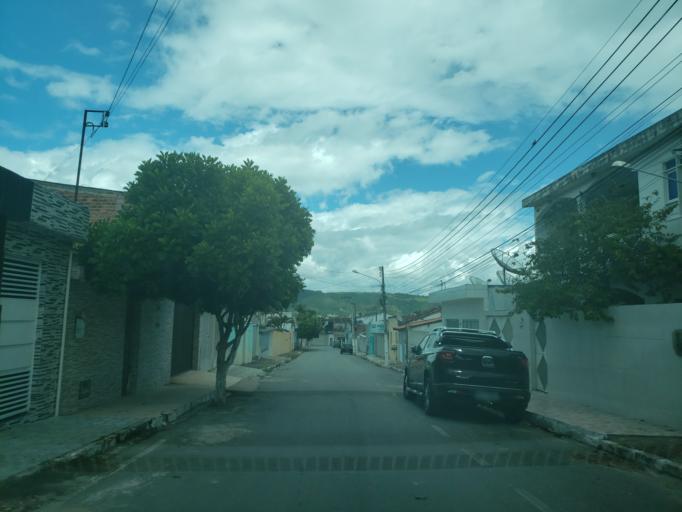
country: BR
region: Alagoas
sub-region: Uniao Dos Palmares
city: Uniao dos Palmares
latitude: -9.1582
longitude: -36.0313
